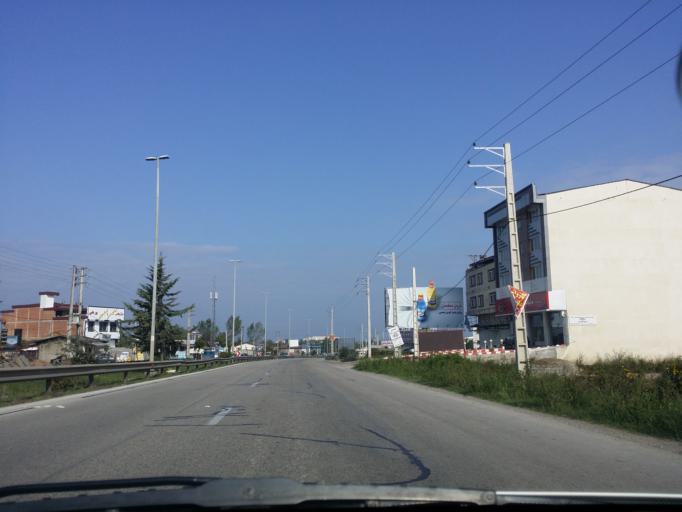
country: IR
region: Mazandaran
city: Chalus
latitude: 36.6689
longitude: 51.3962
